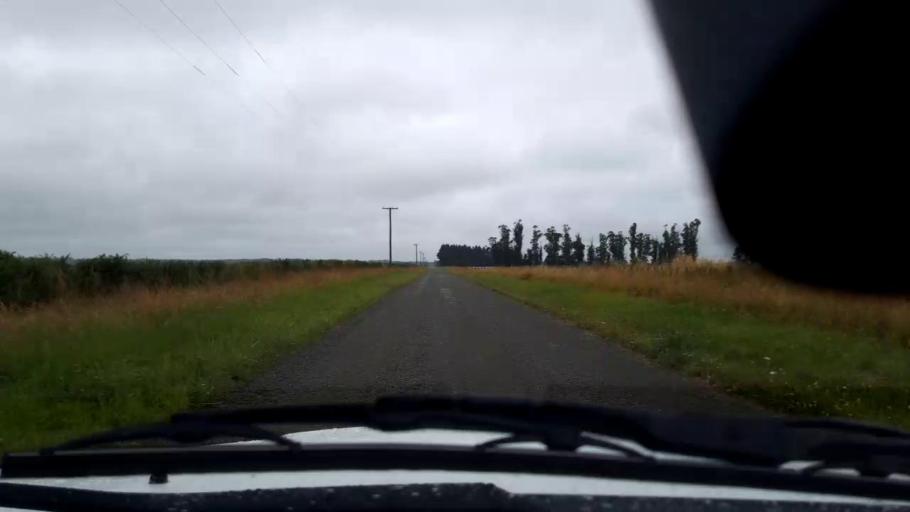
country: NZ
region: Canterbury
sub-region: Timaru District
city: Pleasant Point
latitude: -44.2346
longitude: 171.2023
